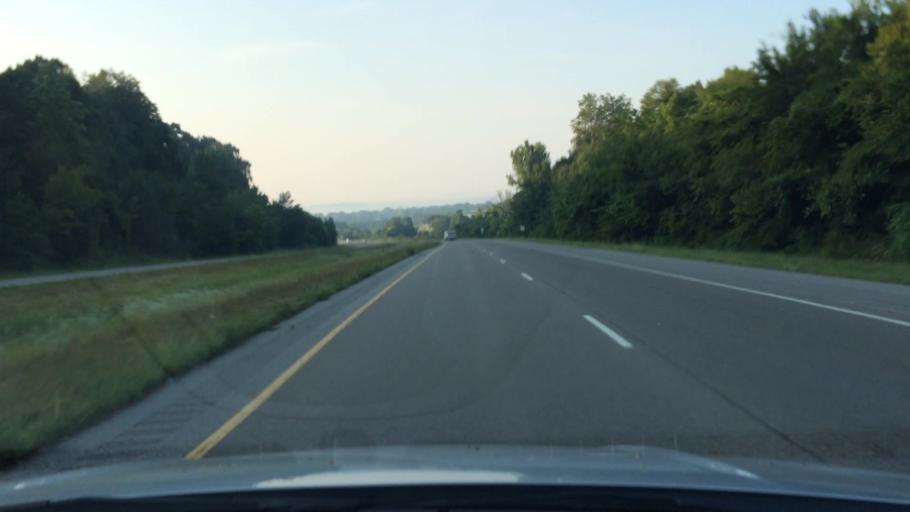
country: US
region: Tennessee
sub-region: Giles County
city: Pulaski
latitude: 35.1775
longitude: -87.0601
